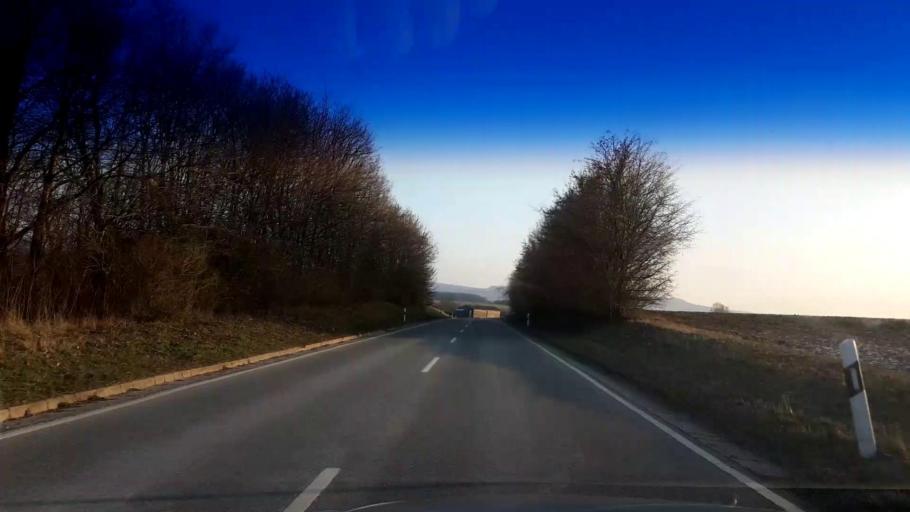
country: DE
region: Bavaria
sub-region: Upper Franconia
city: Schesslitz
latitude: 50.0095
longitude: 11.0123
